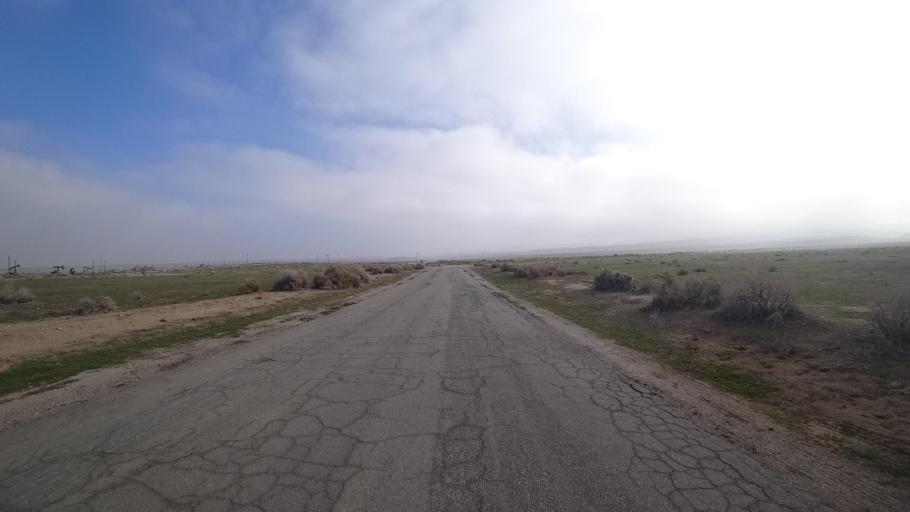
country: US
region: California
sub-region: Kern County
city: Maricopa
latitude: 35.0282
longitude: -119.3402
